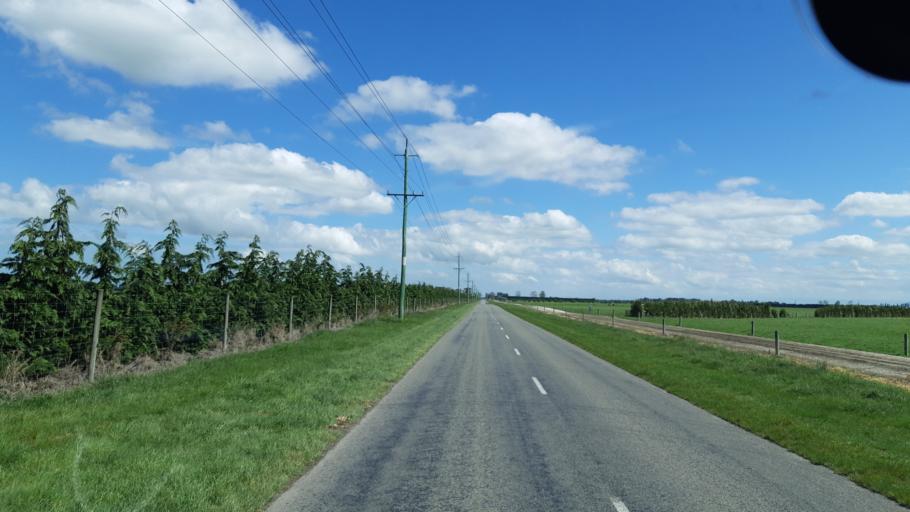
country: NZ
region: Canterbury
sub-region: Ashburton District
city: Tinwald
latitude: -43.9694
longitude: 171.4508
